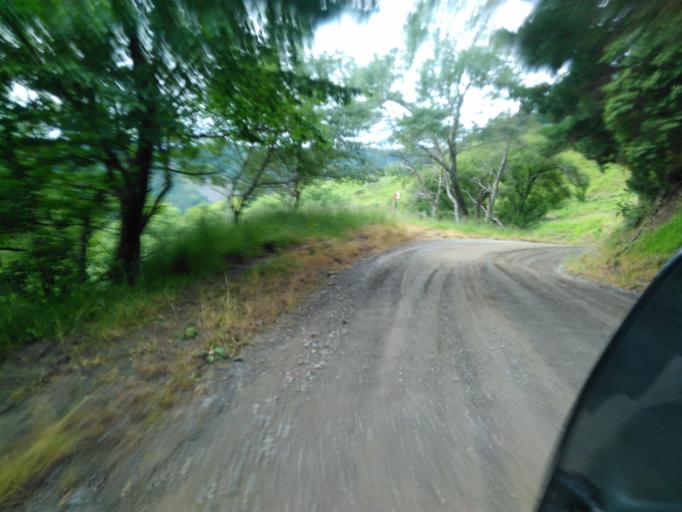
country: NZ
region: Gisborne
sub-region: Gisborne District
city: Gisborne
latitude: -38.0516
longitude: 178.1134
